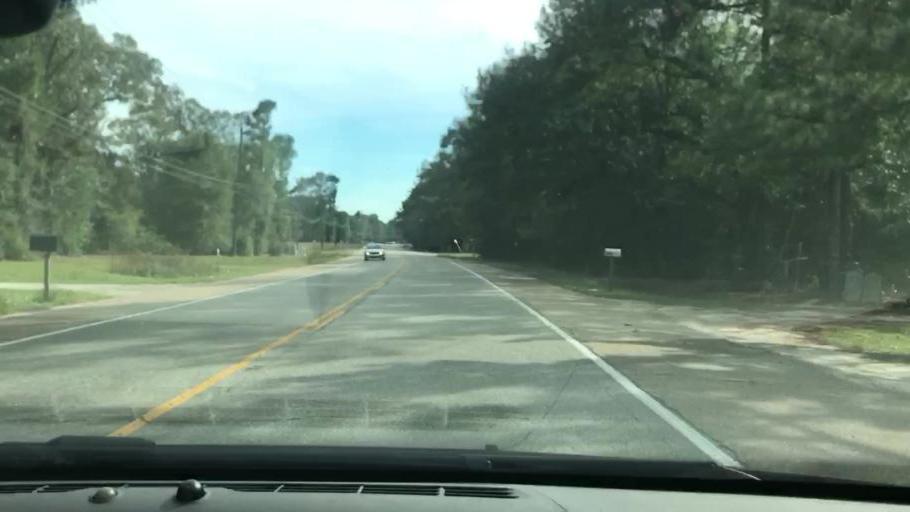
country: US
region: Louisiana
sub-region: Saint Tammany Parish
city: Pearl River
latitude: 30.4070
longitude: -89.7725
